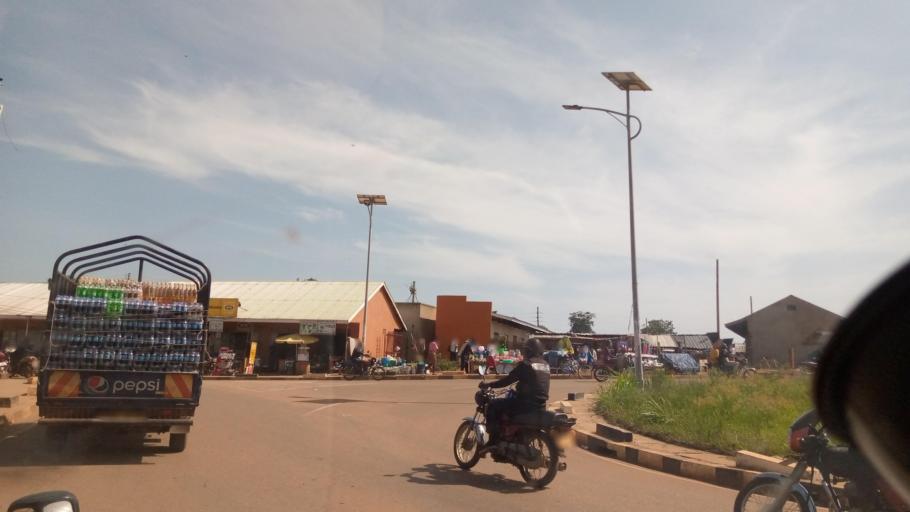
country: UG
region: Northern Region
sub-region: Gulu District
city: Gulu
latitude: 2.7664
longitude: 32.2929
